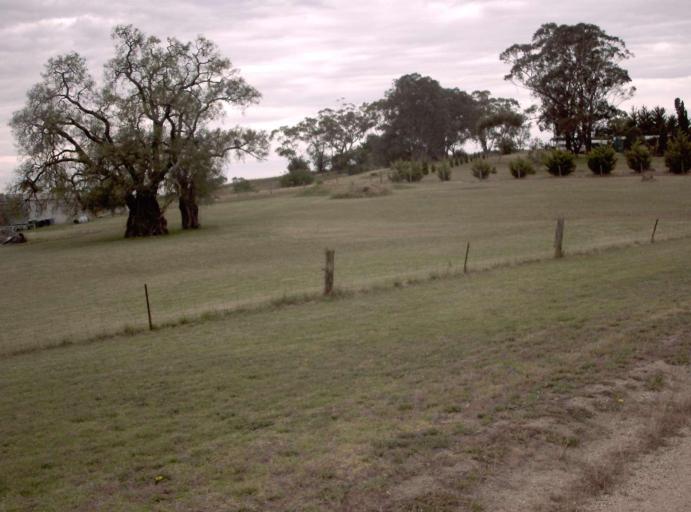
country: AU
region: Victoria
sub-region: Wellington
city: Sale
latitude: -38.1642
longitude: 147.0983
